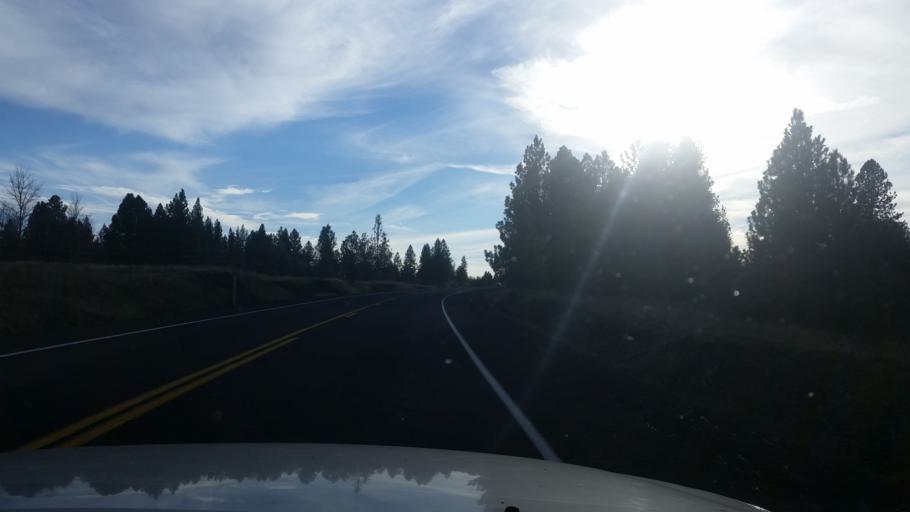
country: US
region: Washington
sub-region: Spokane County
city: Cheney
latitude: 47.3863
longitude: -117.5797
